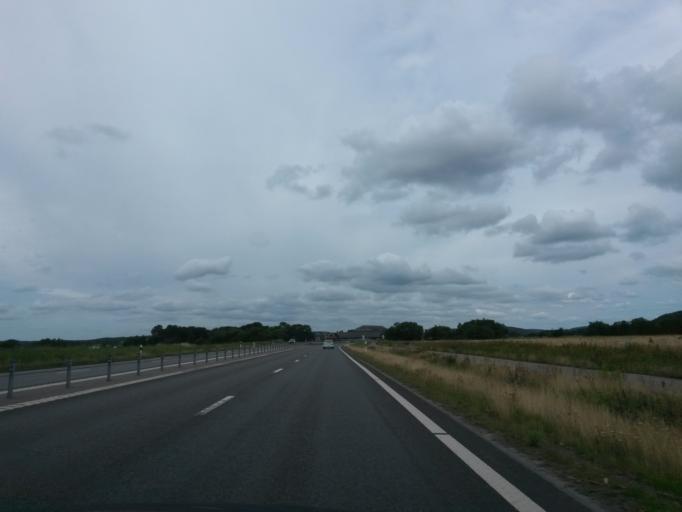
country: SE
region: Halland
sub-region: Varbergs Kommun
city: Varberg
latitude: 57.1375
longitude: 12.2637
